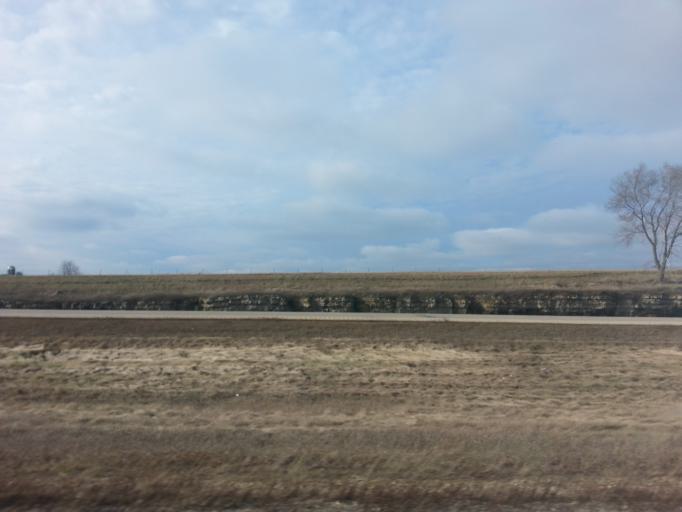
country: US
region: Illinois
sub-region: Winnebago County
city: Cherry Valley
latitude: 42.1743
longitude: -89.0236
